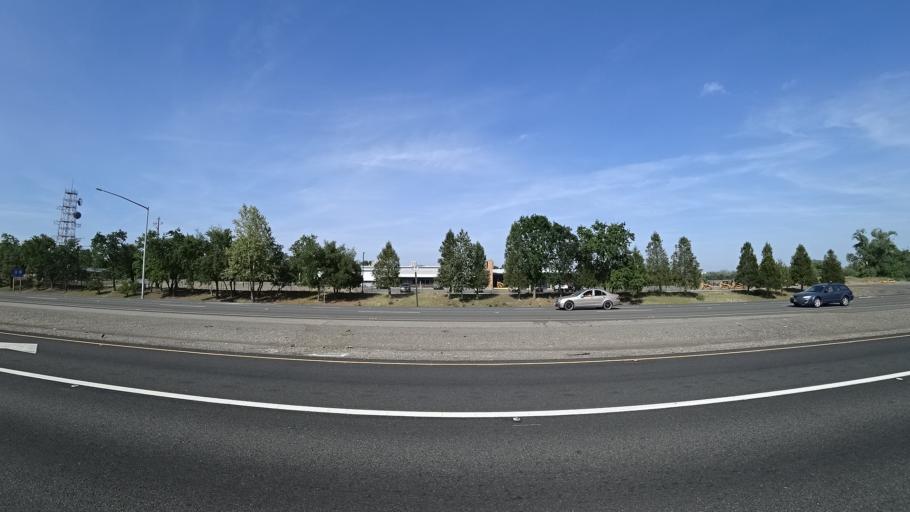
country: US
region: California
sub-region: Butte County
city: Durham
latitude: 39.7017
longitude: -121.7866
